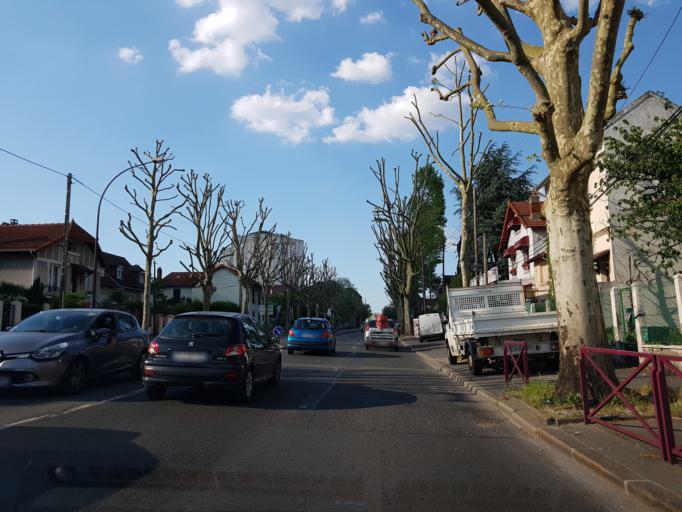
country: FR
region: Ile-de-France
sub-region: Departement du Val-de-Marne
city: L'Hay-les-Roses
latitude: 48.7765
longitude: 2.3402
